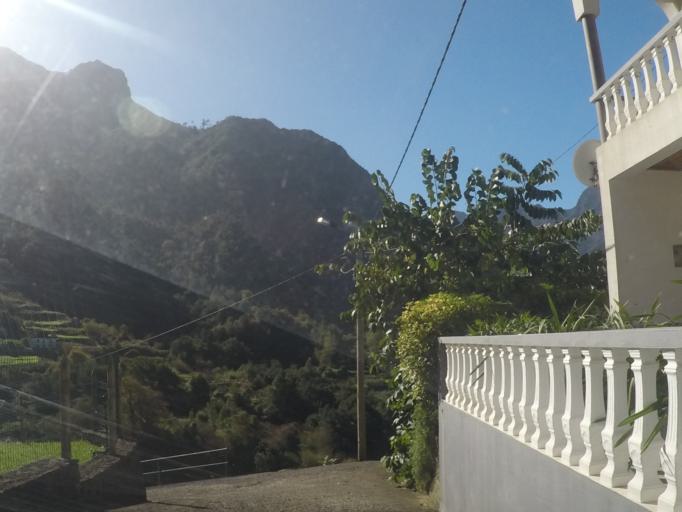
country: PT
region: Madeira
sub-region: Santana
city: Santana
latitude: 32.8003
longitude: -16.9609
